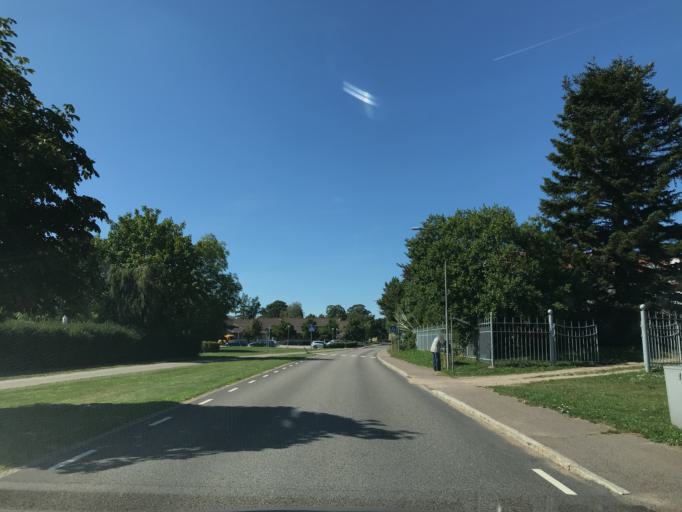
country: SE
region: Skane
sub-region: Tomelilla Kommun
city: Tomelilla
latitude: 55.6524
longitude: 13.8959
